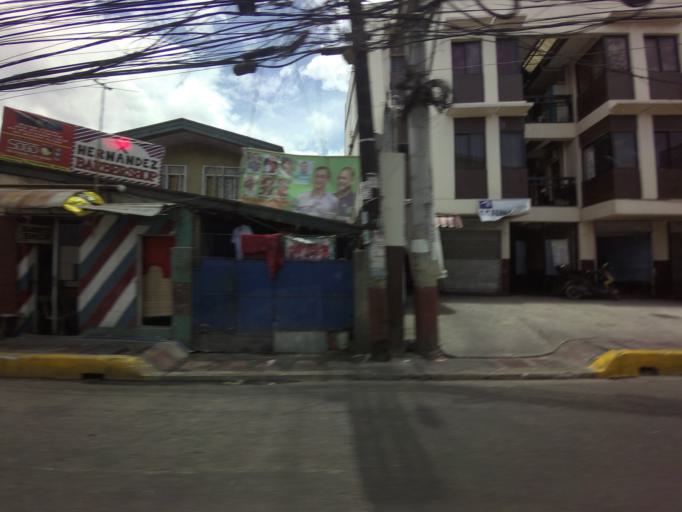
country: PH
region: Metro Manila
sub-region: Marikina
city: Calumpang
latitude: 14.6028
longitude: 121.0934
